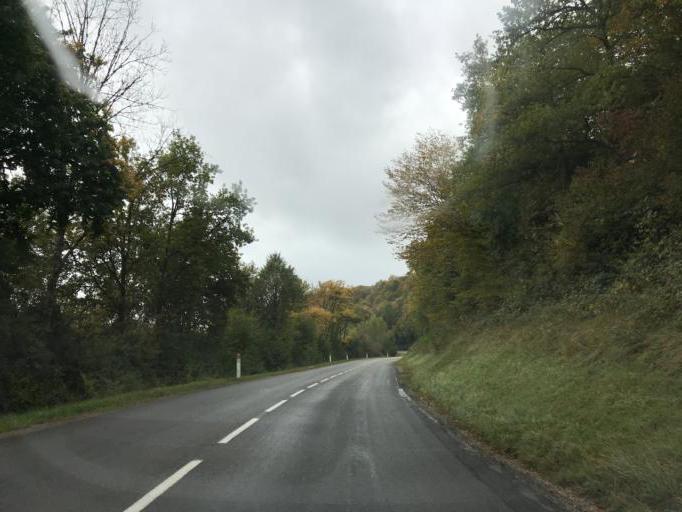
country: FR
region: Franche-Comte
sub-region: Departement du Jura
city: Orgelet
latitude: 46.4930
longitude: 5.5855
